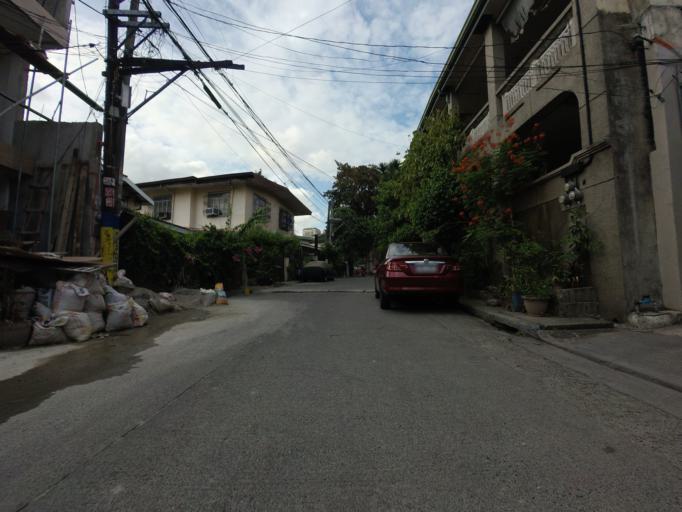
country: PH
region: Metro Manila
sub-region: Mandaluyong
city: Mandaluyong City
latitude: 14.5705
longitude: 121.0405
